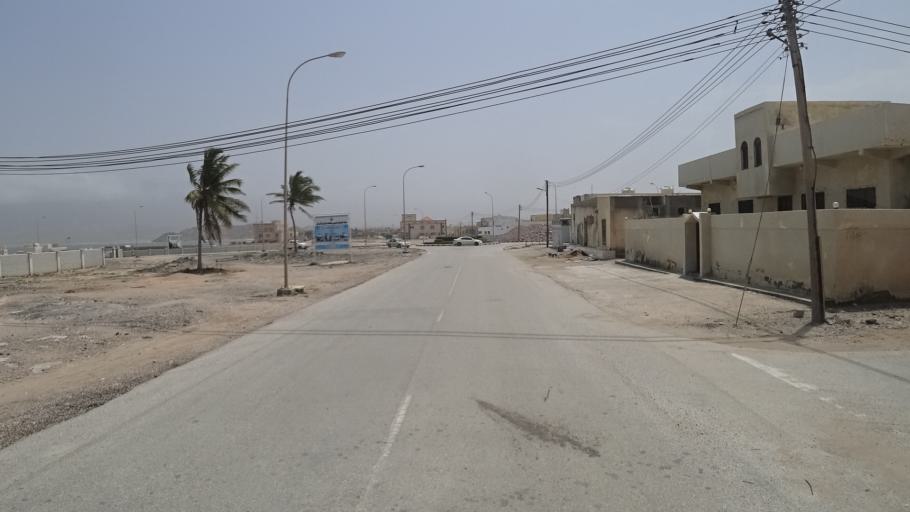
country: OM
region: Zufar
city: Salalah
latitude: 16.9825
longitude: 54.6884
